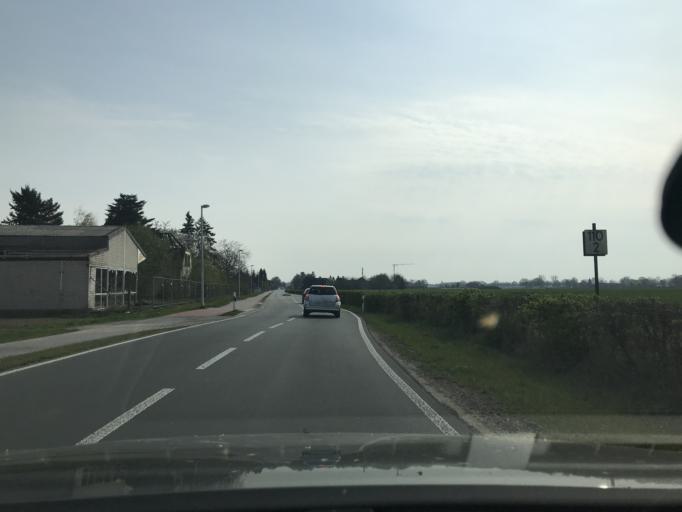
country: DE
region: North Rhine-Westphalia
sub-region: Regierungsbezirk Dusseldorf
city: Goch
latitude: 51.7238
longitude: 6.1662
